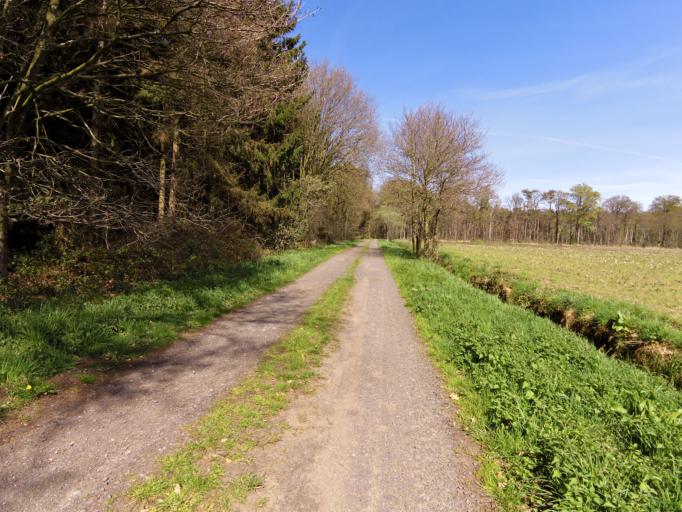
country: BE
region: Flanders
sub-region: Provincie West-Vlaanderen
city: Jabbeke
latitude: 51.1535
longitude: 3.0881
